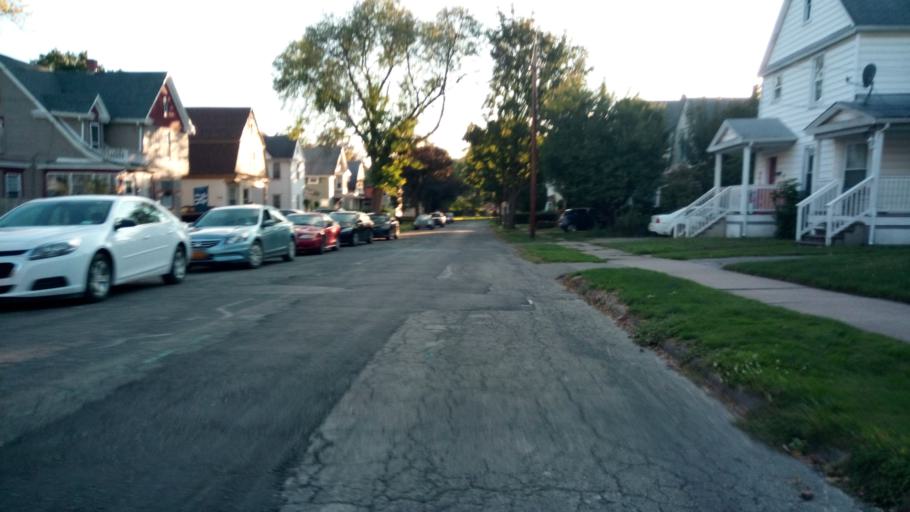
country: US
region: New York
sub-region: Chemung County
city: Elmira
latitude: 42.0987
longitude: -76.8179
